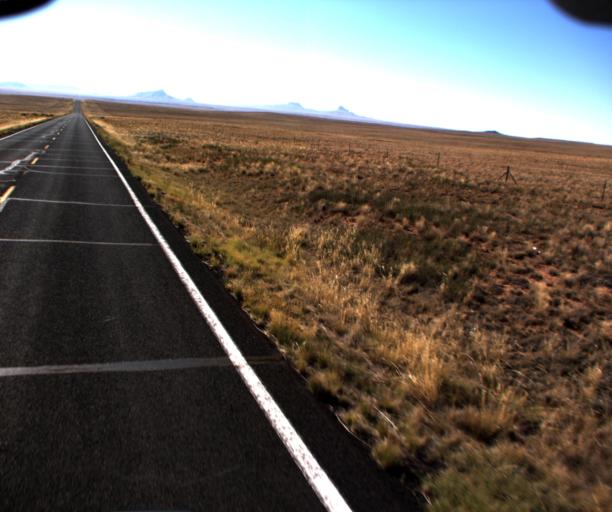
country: US
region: Arizona
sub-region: Navajo County
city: First Mesa
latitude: 35.6302
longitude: -110.4819
